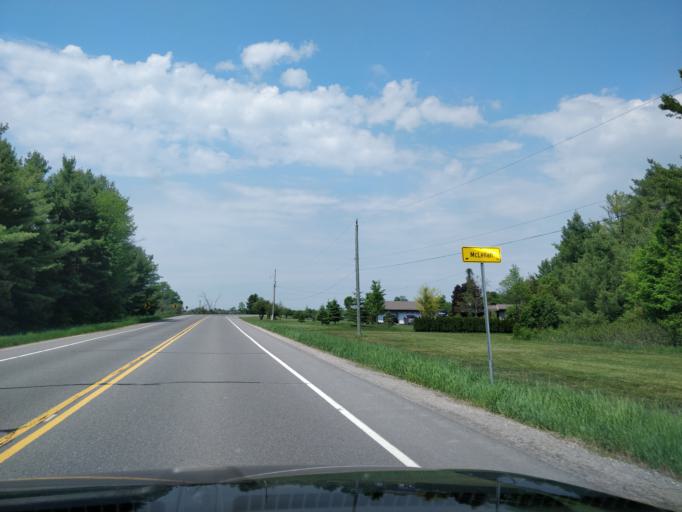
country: CA
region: Ontario
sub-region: Lanark County
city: Smiths Falls
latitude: 45.0211
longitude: -76.0796
